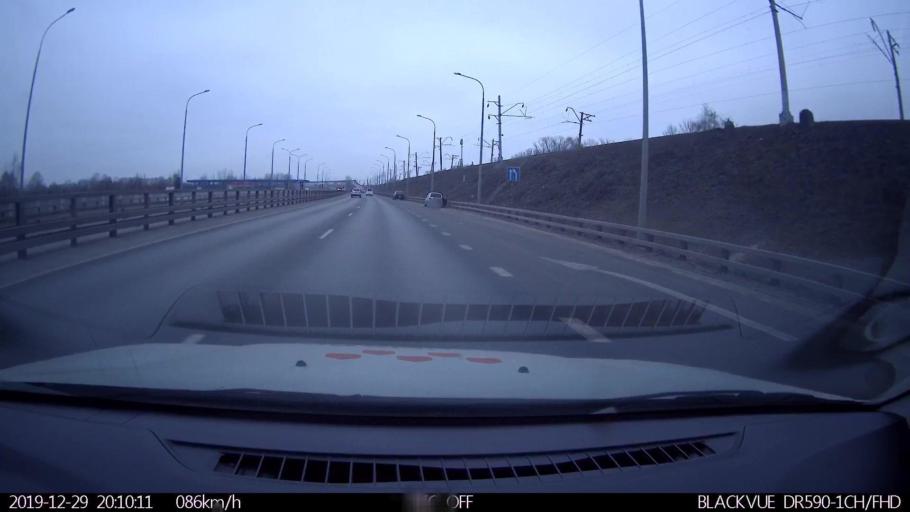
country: RU
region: Nizjnij Novgorod
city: Neklyudovo
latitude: 56.3685
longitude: 43.9402
